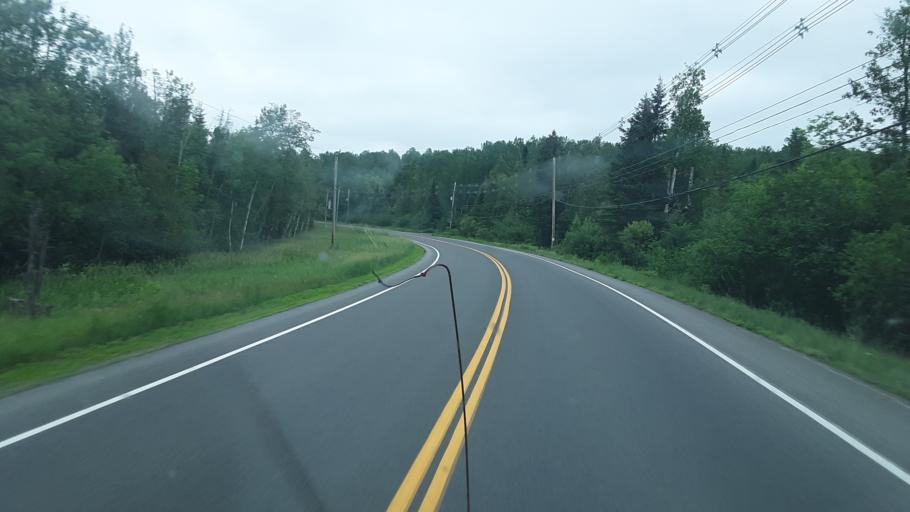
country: US
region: Maine
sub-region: Penobscot County
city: Patten
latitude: 45.8884
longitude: -68.4233
